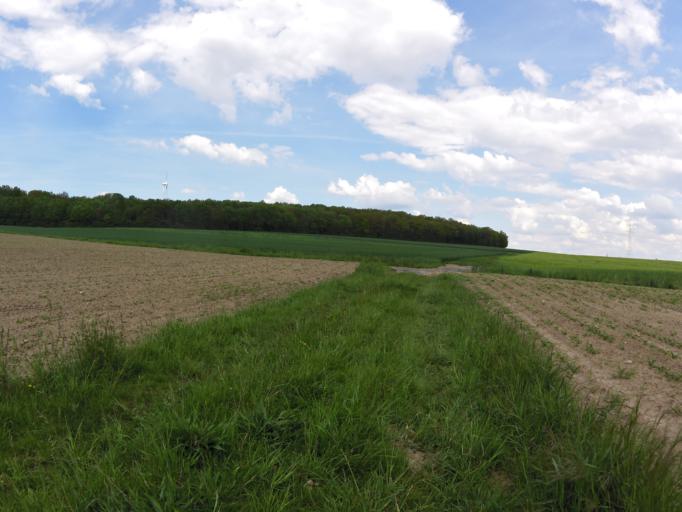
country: DE
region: Bavaria
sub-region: Regierungsbezirk Unterfranken
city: Theilheim
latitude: 49.7406
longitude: 10.0405
